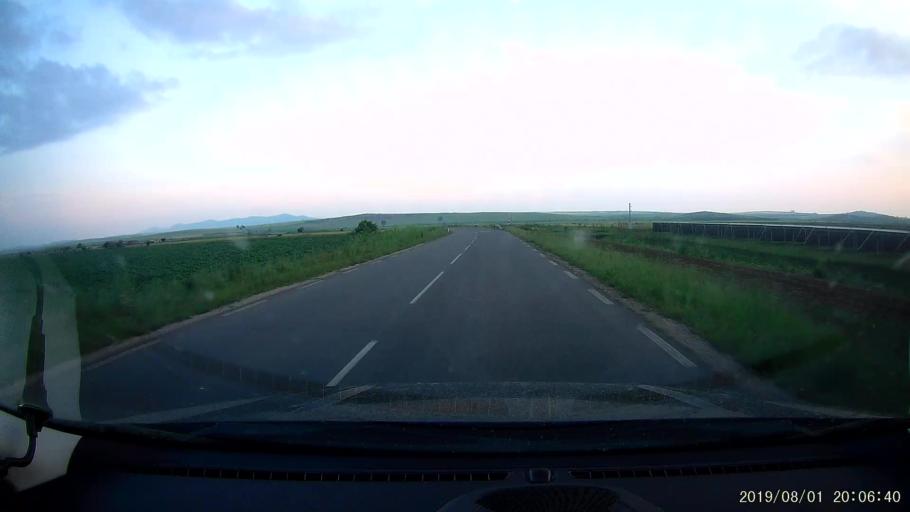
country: BG
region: Yambol
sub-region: Obshtina Yambol
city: Yambol
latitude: 42.5321
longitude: 26.5572
